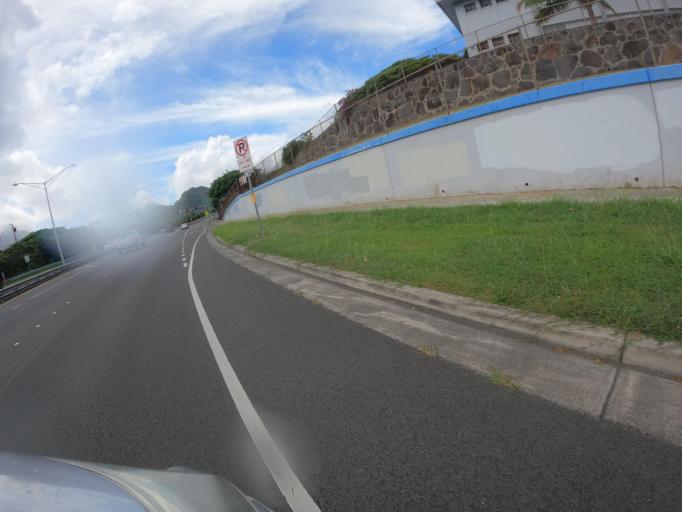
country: US
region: Hawaii
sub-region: Honolulu County
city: Kailua
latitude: 21.4075
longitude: -157.7574
